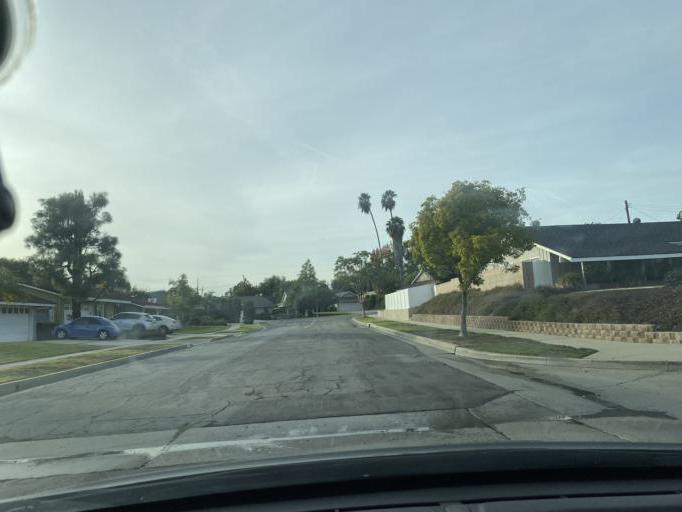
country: US
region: California
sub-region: Orange County
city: Placentia
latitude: 33.8973
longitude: -117.8791
